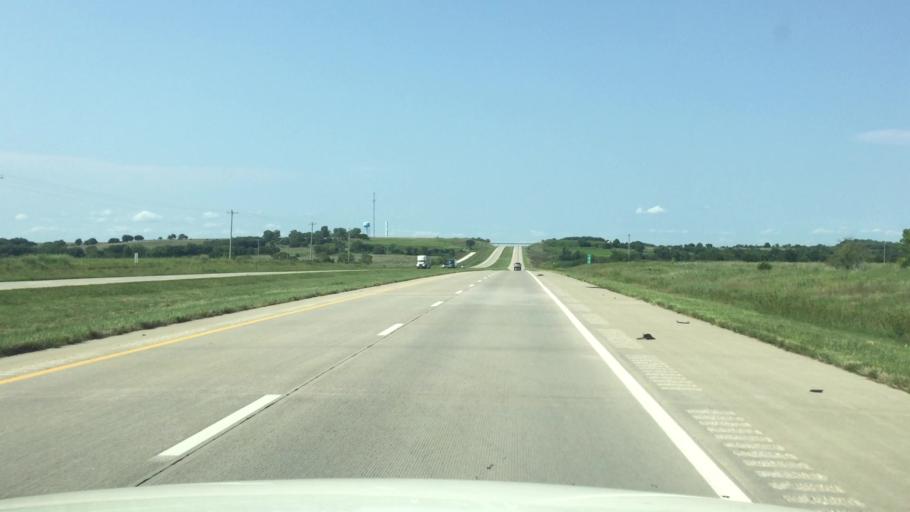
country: US
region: Kansas
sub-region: Linn County
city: Pleasanton
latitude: 38.0923
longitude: -94.7133
